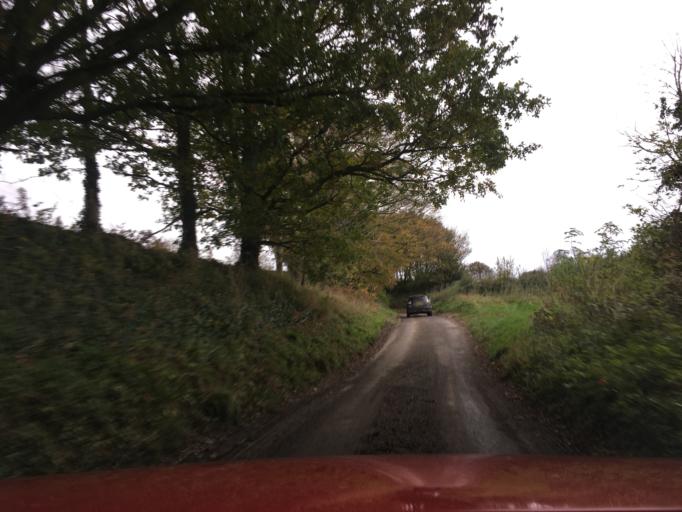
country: GB
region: England
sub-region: Somerset
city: Ilminster
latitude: 50.9535
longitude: -2.8722
